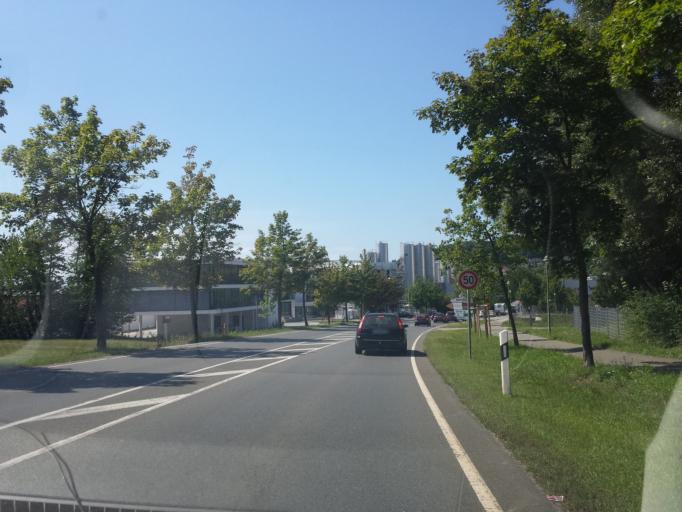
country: DE
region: Bavaria
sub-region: Upper Palatinate
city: Willmering
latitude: 49.2288
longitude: 12.6819
